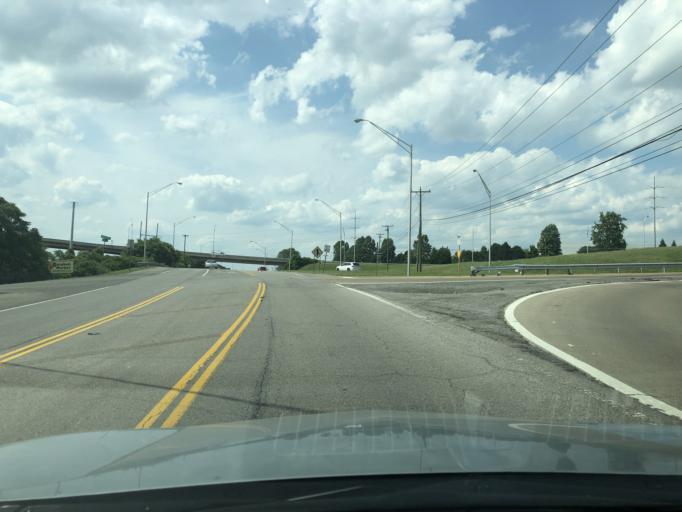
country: US
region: Tennessee
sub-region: Davidson County
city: Oak Hill
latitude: 36.1008
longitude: -86.7612
